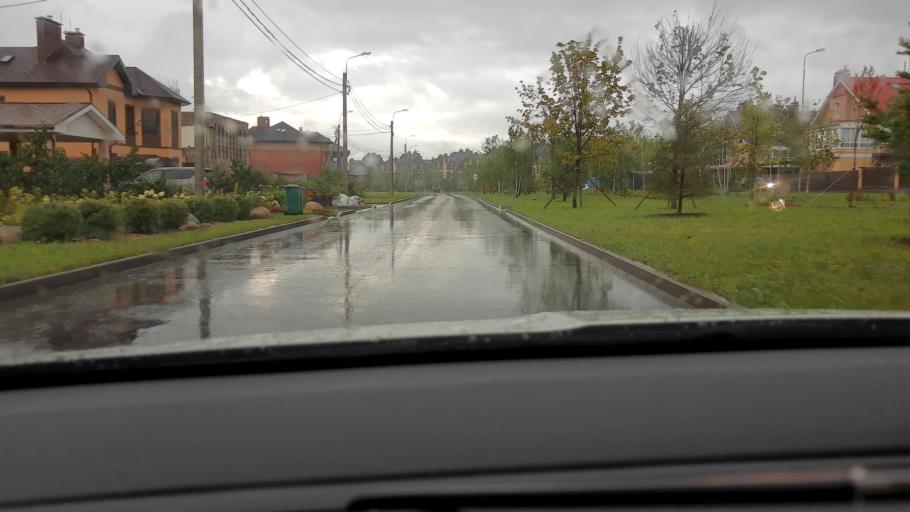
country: RU
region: Moskovskaya
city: Kommunarka
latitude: 55.5370
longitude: 37.4920
